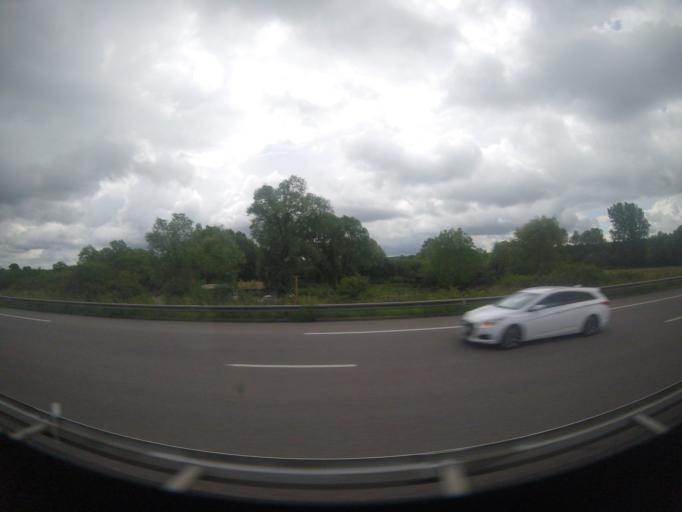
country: FR
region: Lorraine
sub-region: Departement de Meurthe-et-Moselle
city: Conflans-en-Jarnisy
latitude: 49.1588
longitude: 5.7396
